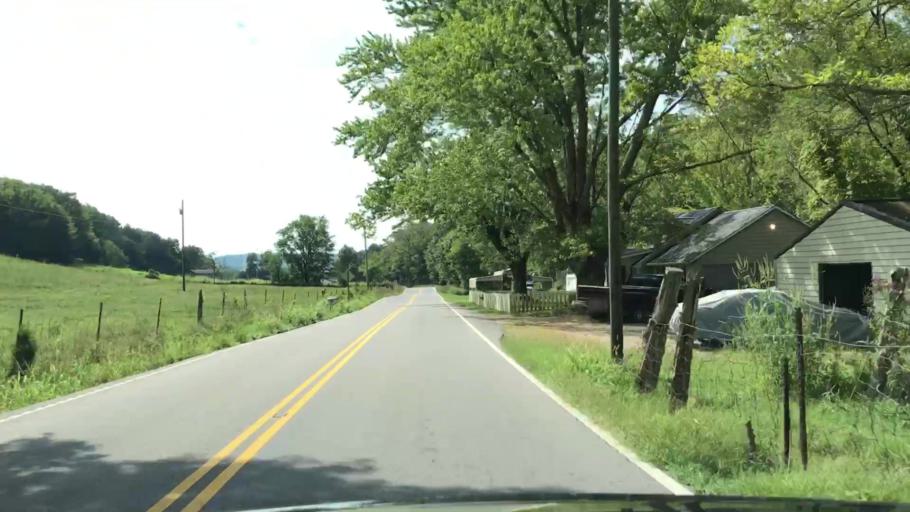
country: US
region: Tennessee
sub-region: Trousdale County
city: Hartsville
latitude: 36.4841
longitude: -86.1877
